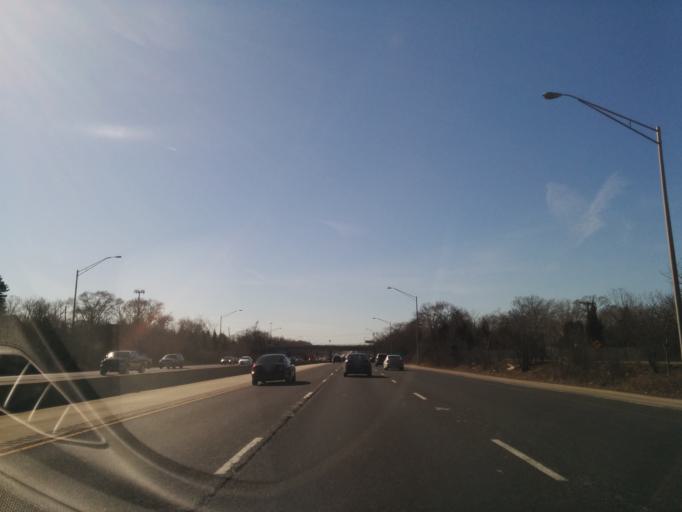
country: US
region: Illinois
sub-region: DuPage County
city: Darien
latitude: 41.7392
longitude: -87.9505
